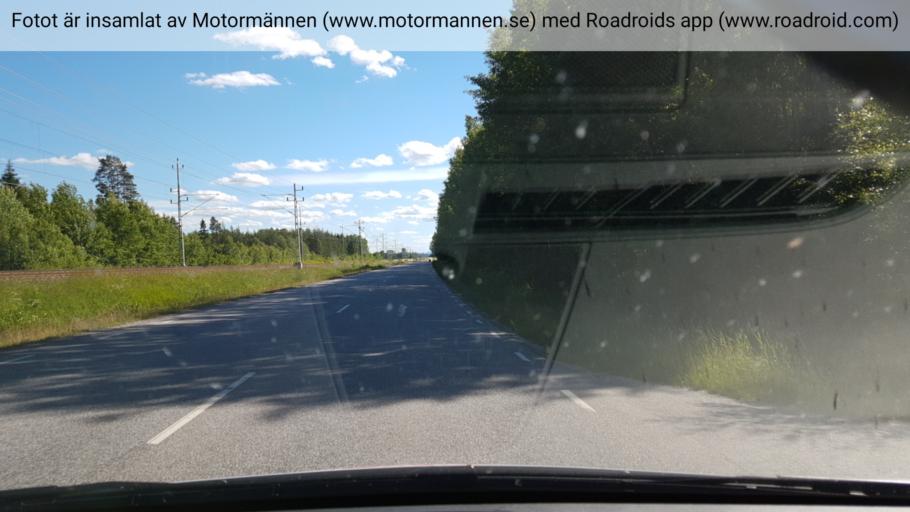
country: SE
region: Vaestra Goetaland
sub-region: Toreboda Kommun
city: Toereboda
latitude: 58.6630
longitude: 14.0893
